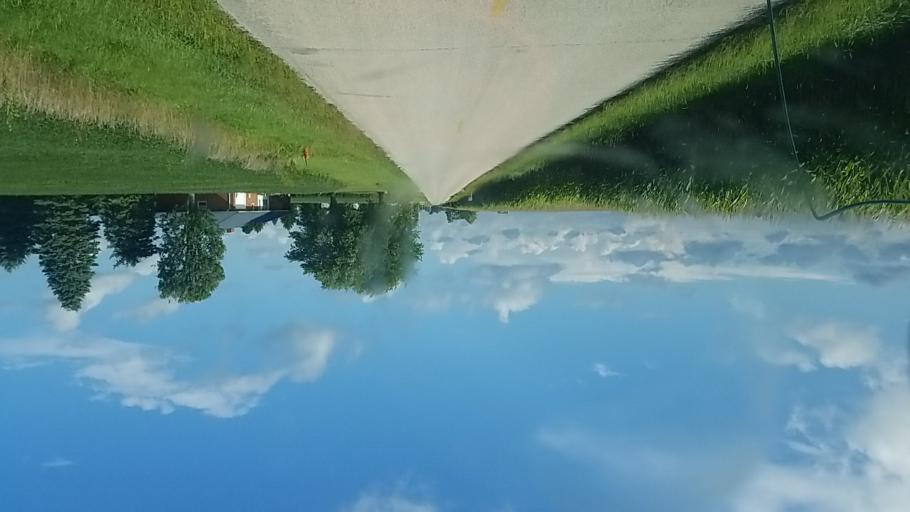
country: US
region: Ohio
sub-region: Hardin County
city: Forest
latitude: 40.7138
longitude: -83.5144
